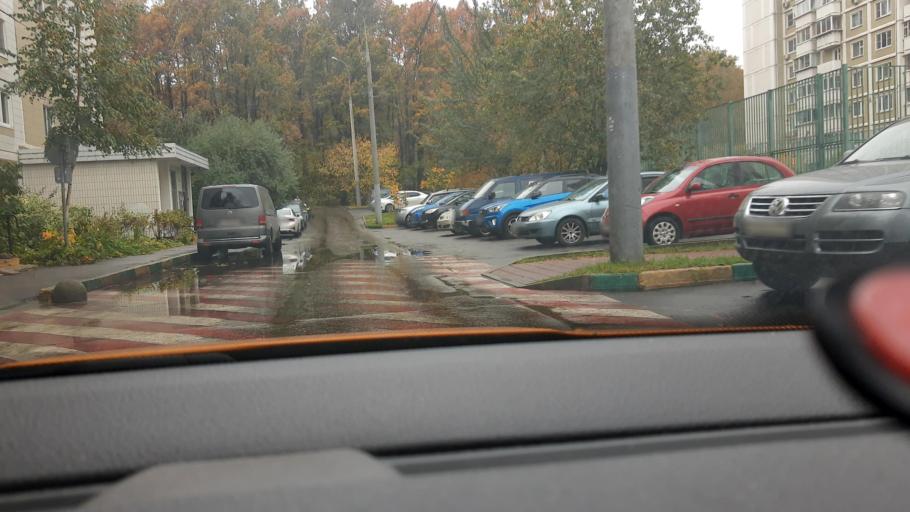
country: RU
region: Moskovskaya
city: Pavshino
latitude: 55.8449
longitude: 37.3470
